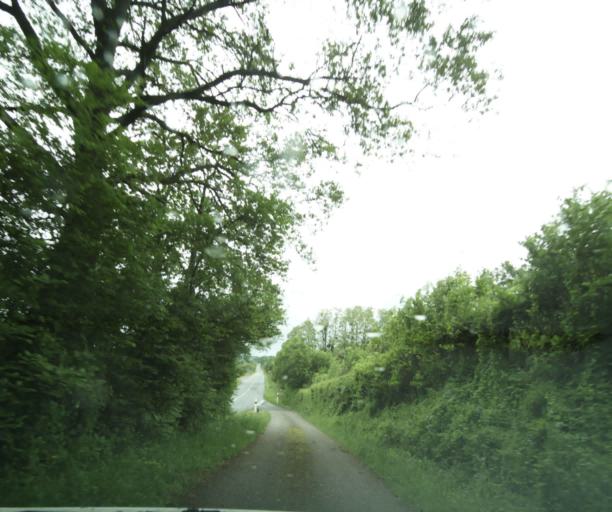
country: FR
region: Bourgogne
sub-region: Departement de Saone-et-Loire
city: Charolles
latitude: 46.4949
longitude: 4.2671
